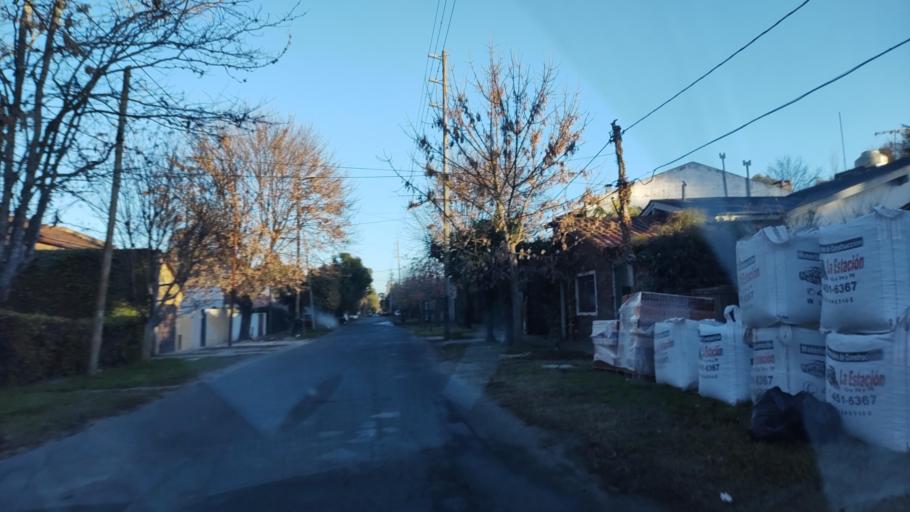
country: AR
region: Buenos Aires
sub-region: Partido de La Plata
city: La Plata
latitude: -34.8885
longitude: -58.0368
